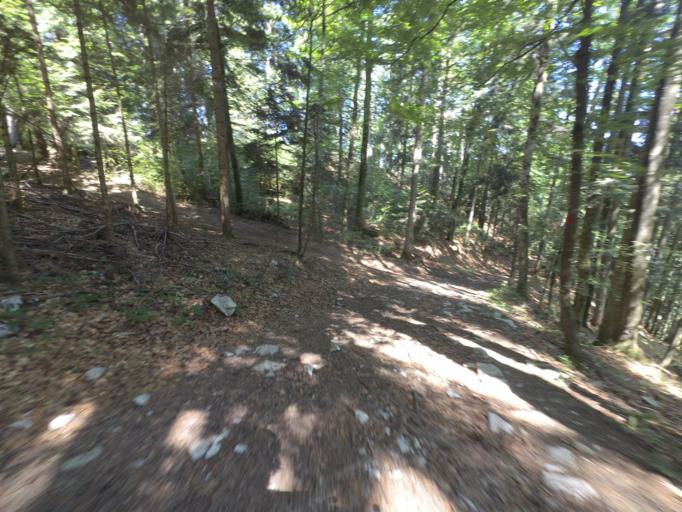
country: AT
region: Salzburg
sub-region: Politischer Bezirk Salzburg-Umgebung
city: Elsbethen
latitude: 47.7577
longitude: 13.1112
